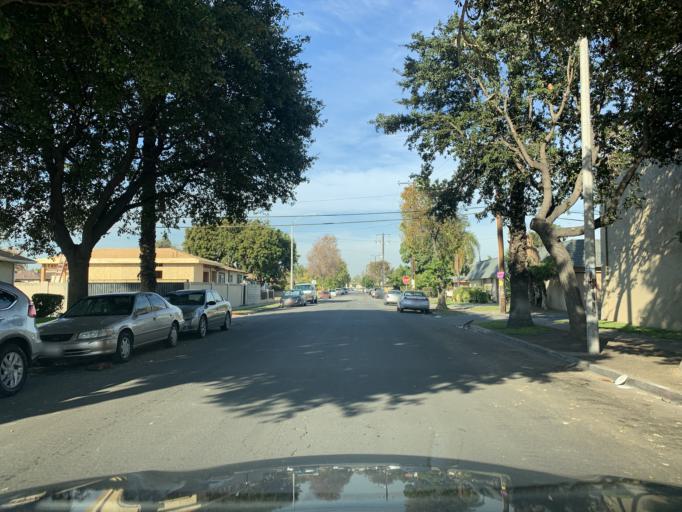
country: US
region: California
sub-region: Orange County
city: Anaheim
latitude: 33.8145
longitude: -117.9090
